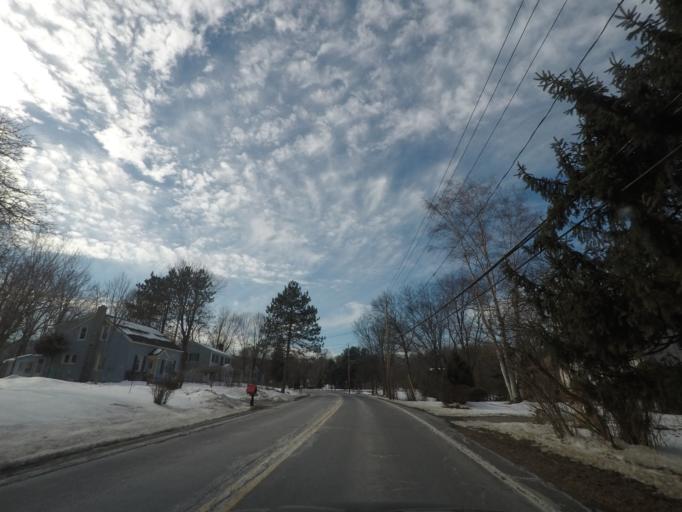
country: US
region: New York
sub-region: Albany County
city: Voorheesville
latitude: 42.6535
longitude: -73.9490
